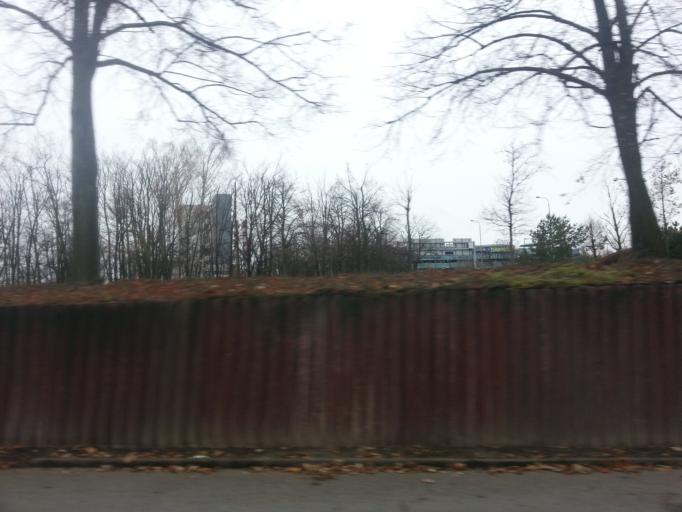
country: CZ
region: Central Bohemia
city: Tuchomerice
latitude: 50.1093
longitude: 14.2745
